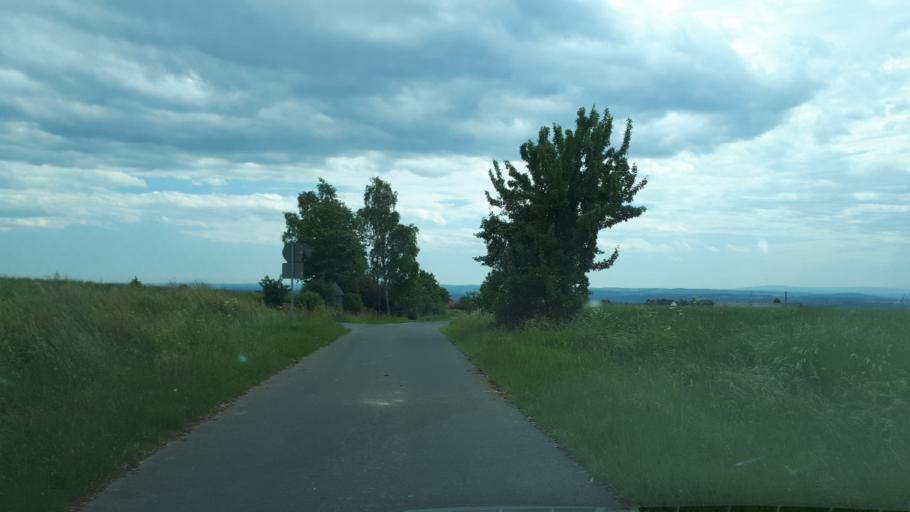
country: DE
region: Rheinland-Pfalz
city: Greimersburg
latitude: 50.1908
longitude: 7.1343
